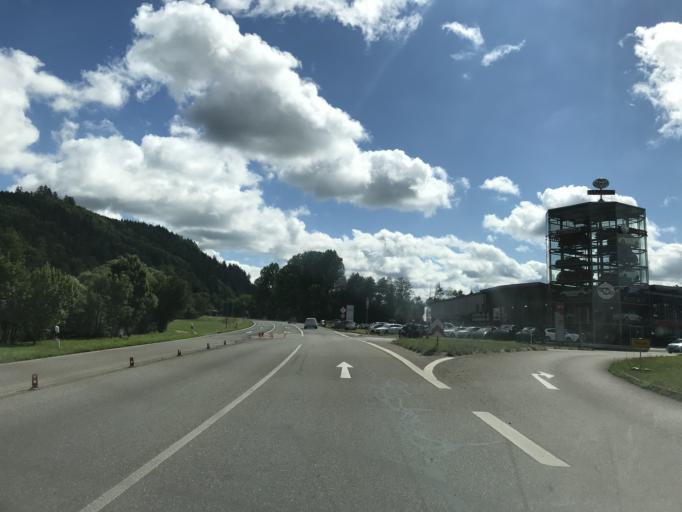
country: DE
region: Baden-Wuerttemberg
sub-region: Freiburg Region
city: Maulburg
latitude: 47.6460
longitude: 7.7695
